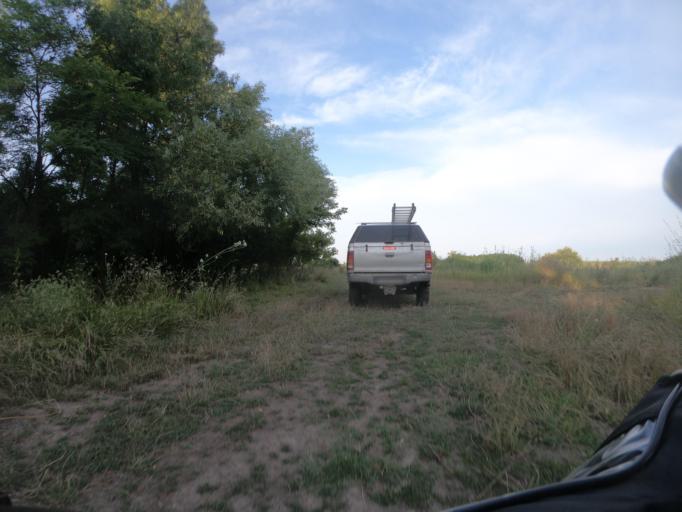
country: HU
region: Borsod-Abauj-Zemplen
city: Mezokeresztes
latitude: 47.7658
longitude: 20.7904
